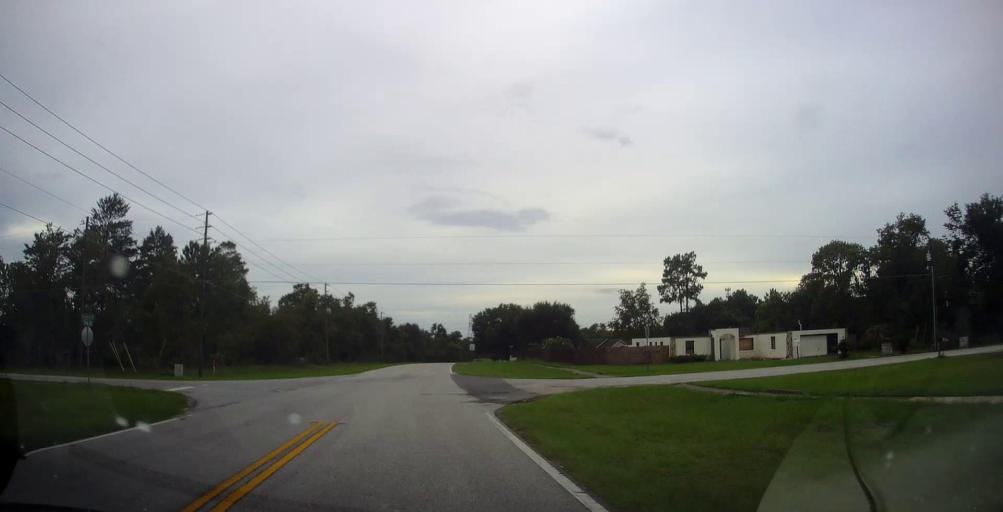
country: US
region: Florida
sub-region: Marion County
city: Silver Springs Shores
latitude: 29.1325
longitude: -82.0324
